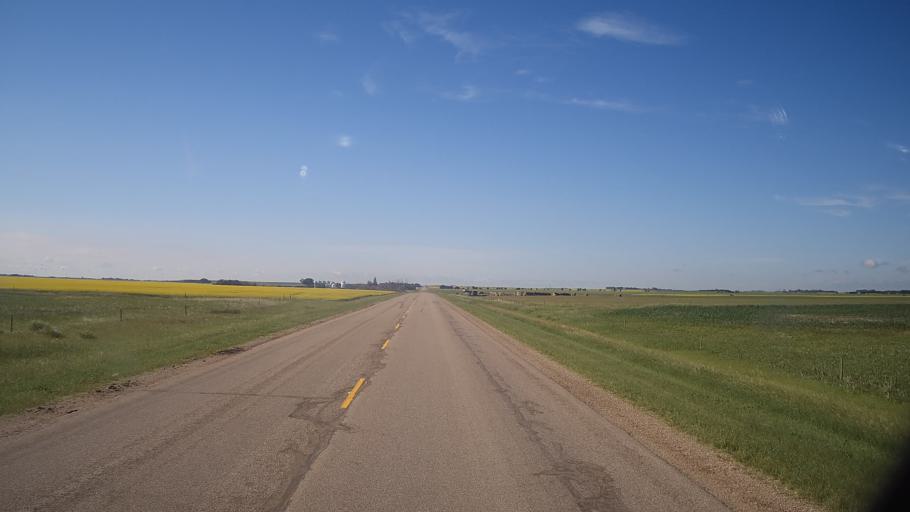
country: CA
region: Saskatchewan
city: Watrous
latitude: 51.6867
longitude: -105.3809
